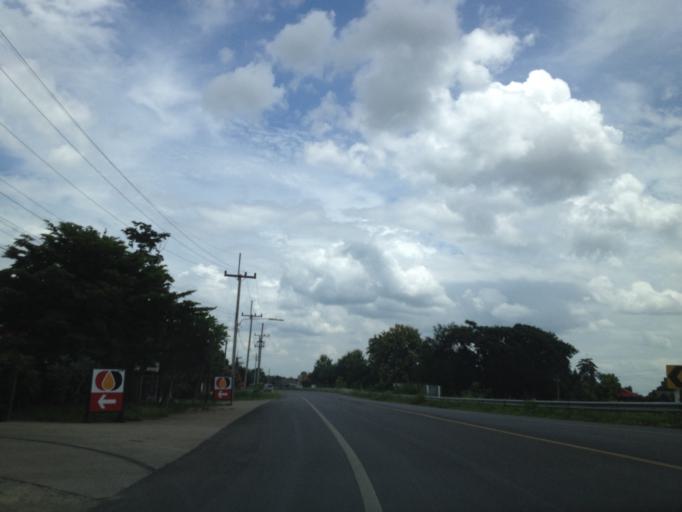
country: TH
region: Chiang Mai
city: San Pa Tong
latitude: 18.6322
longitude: 98.8695
